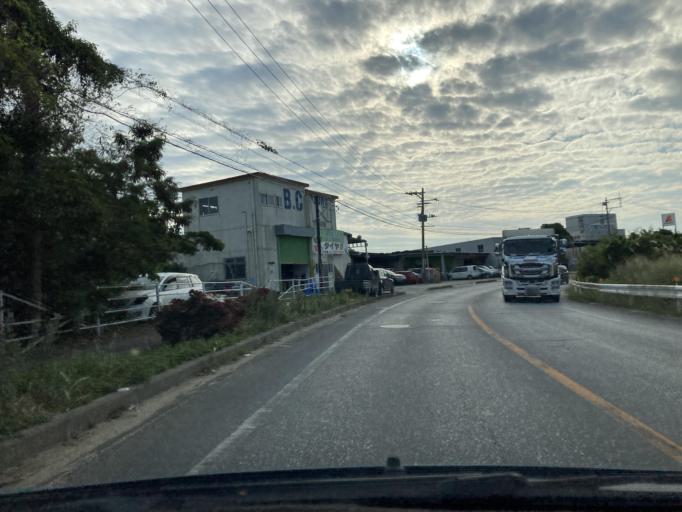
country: JP
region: Okinawa
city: Okinawa
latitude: 26.3659
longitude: 127.8057
